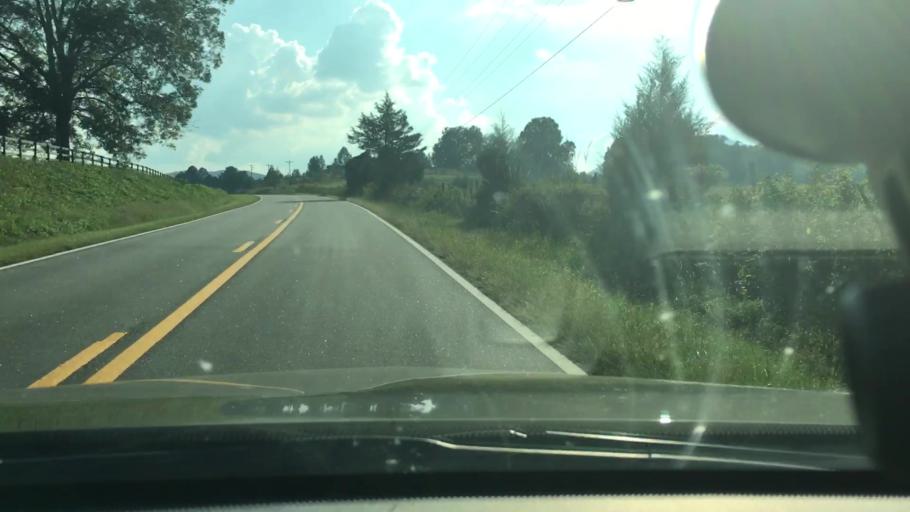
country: US
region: North Carolina
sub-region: Polk County
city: Columbus
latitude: 35.3081
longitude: -82.1506
